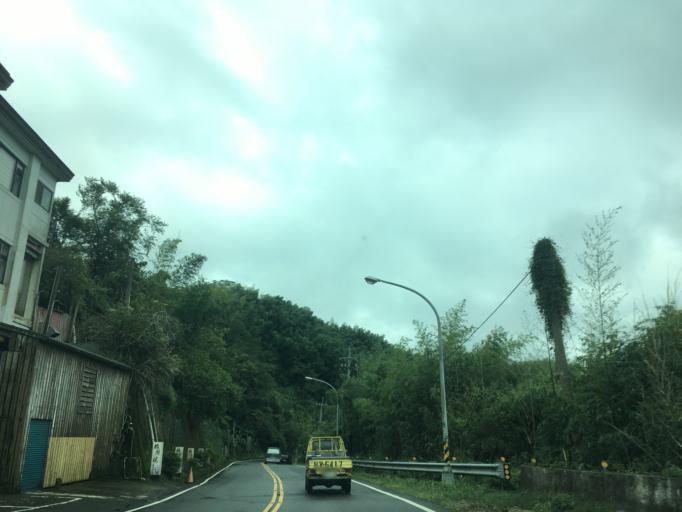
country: TW
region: Taiwan
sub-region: Chiayi
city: Jiayi Shi
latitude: 23.4419
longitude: 120.6707
